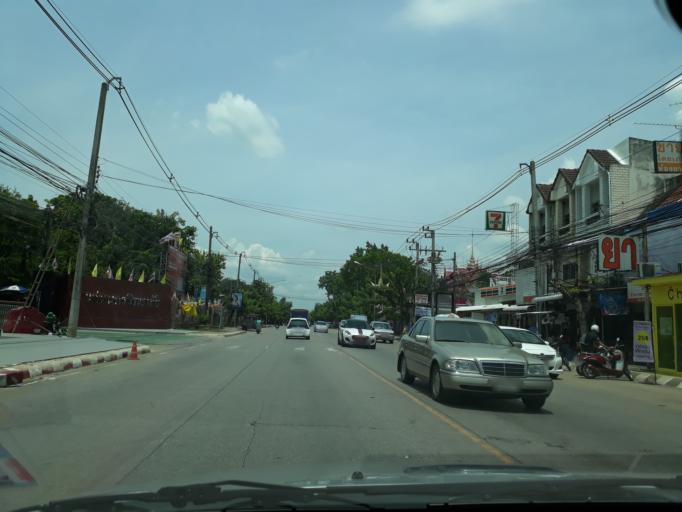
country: TH
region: Khon Kaen
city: Khon Kaen
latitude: 16.4151
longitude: 102.8242
